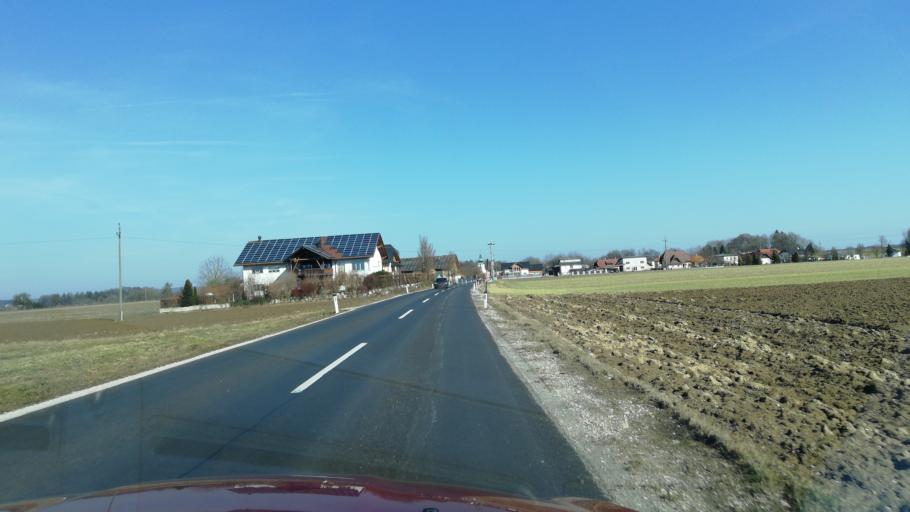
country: AT
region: Upper Austria
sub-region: Politischer Bezirk Vocklabruck
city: Desselbrunn
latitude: 48.0179
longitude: 13.7654
